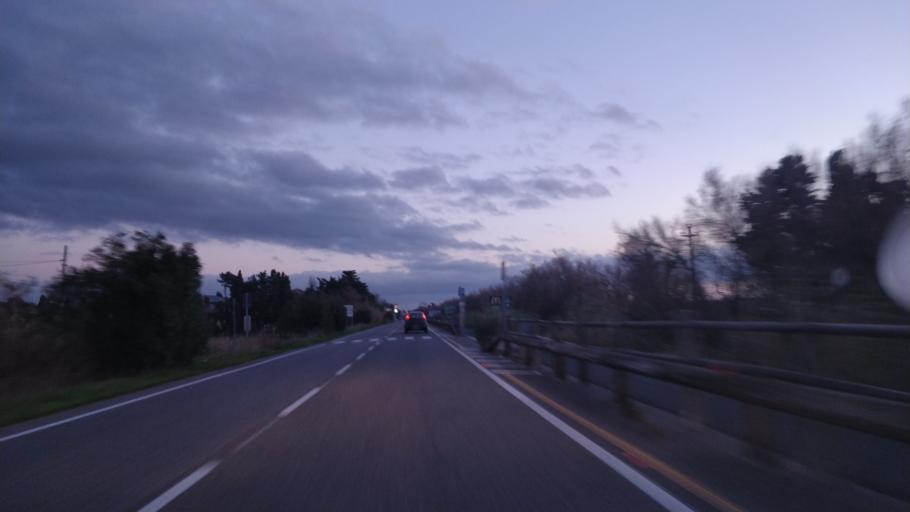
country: IT
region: Tuscany
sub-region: Provincia di Livorno
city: Vada
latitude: 43.3664
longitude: 10.4514
